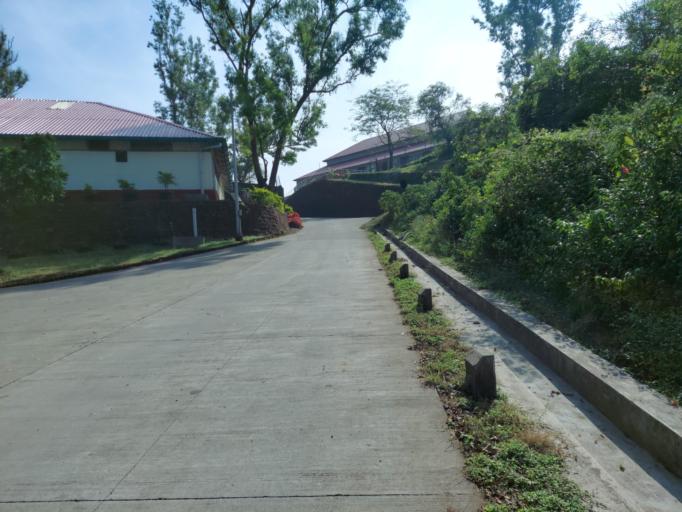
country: IN
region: Maharashtra
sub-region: Pune Division
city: Sasvad
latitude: 18.2814
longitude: 73.9833
